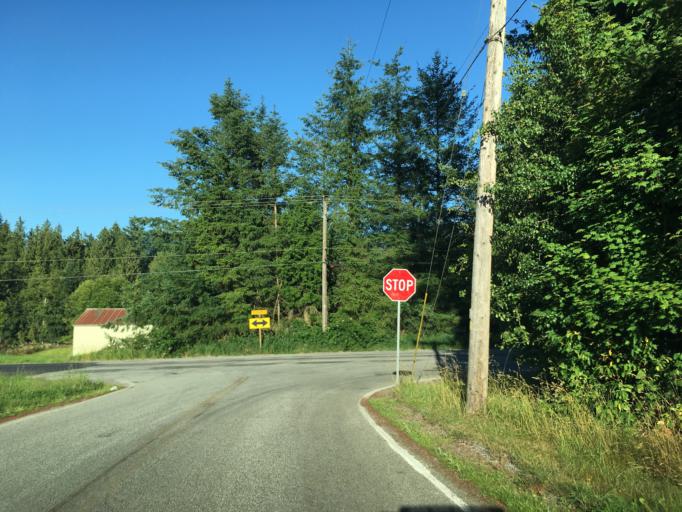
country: US
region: Washington
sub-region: Whatcom County
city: Nooksack
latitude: 48.9420
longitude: -122.2823
